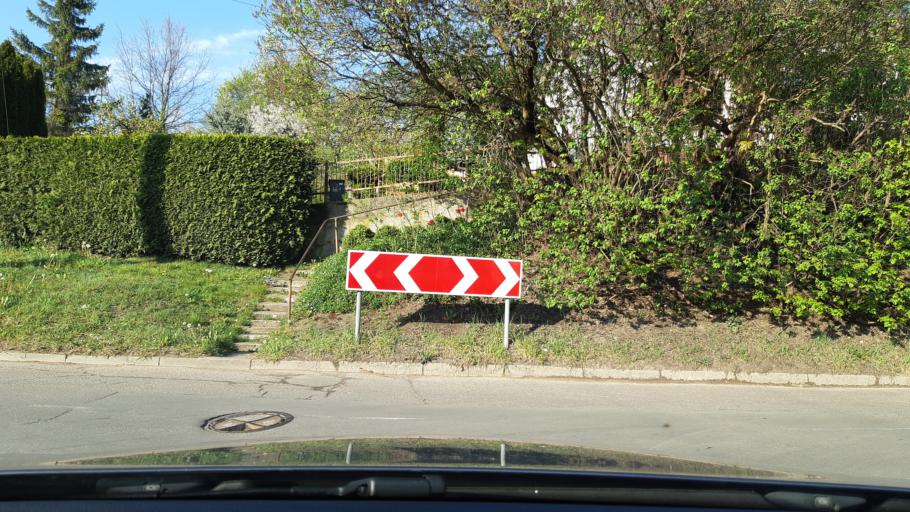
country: LT
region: Kauno apskritis
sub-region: Kaunas
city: Aleksotas
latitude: 54.8748
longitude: 23.9427
